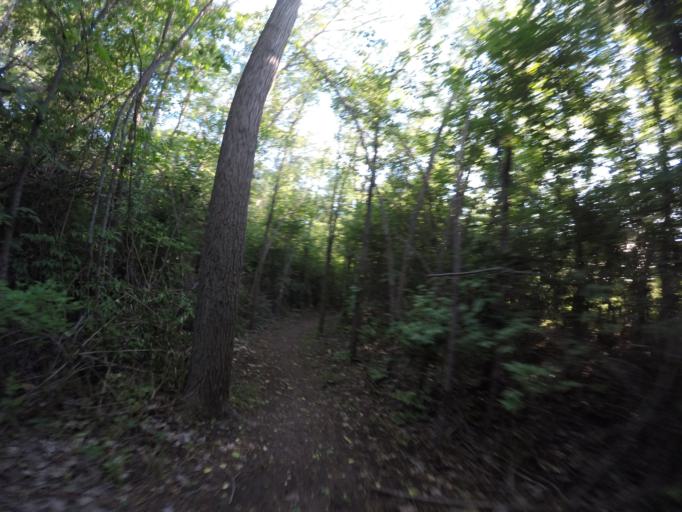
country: US
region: Kansas
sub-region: Riley County
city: Manhattan
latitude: 39.1724
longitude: -96.5579
